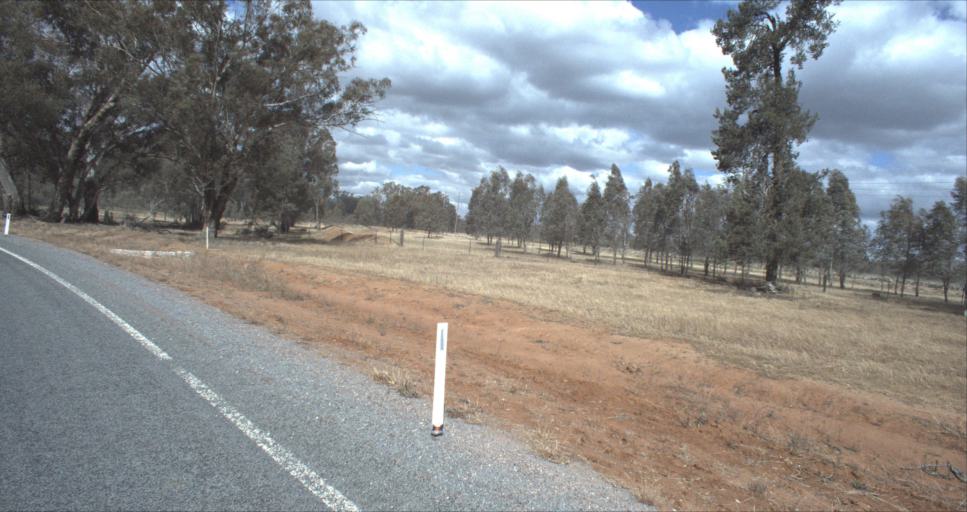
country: AU
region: New South Wales
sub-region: Leeton
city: Leeton
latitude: -34.6436
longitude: 146.3559
